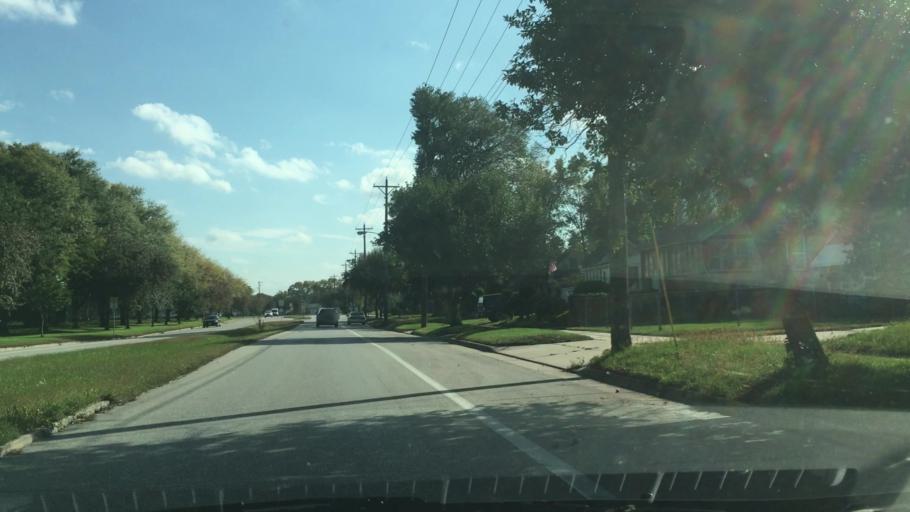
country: US
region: Minnesota
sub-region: Olmsted County
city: Rochester
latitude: 44.0065
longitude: -92.4487
